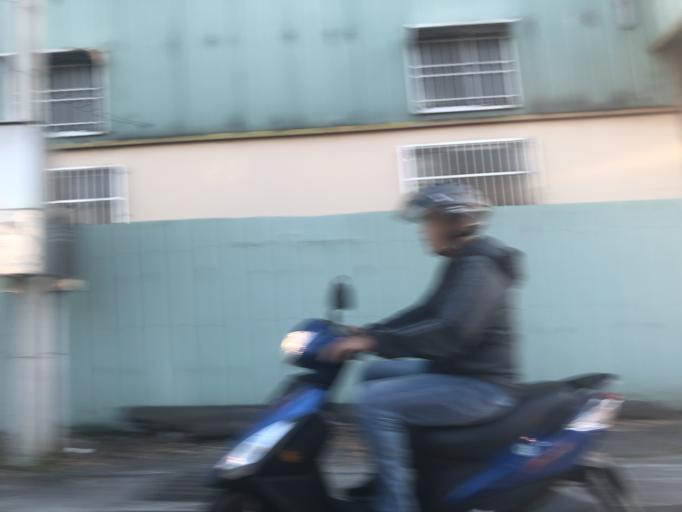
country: TW
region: Taiwan
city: Fengyuan
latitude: 24.2779
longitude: 120.7713
